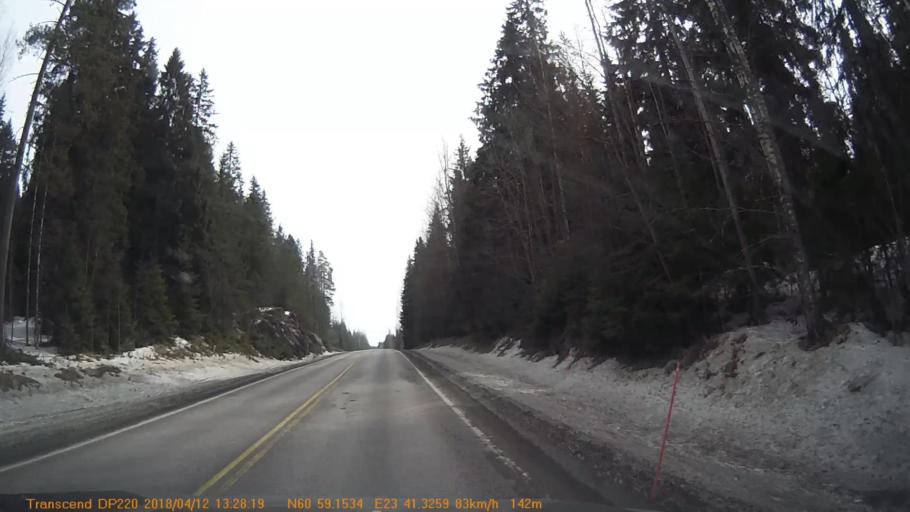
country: FI
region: Pirkanmaa
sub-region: Etelae-Pirkanmaa
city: Kylmaekoski
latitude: 60.9858
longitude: 23.6889
